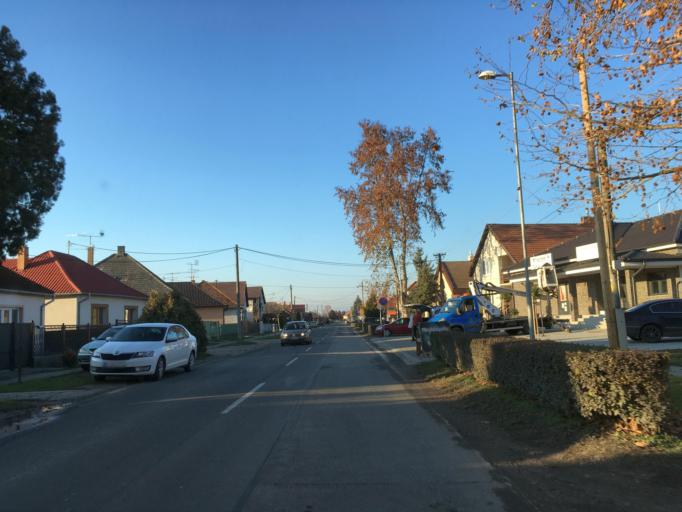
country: SK
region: Trnavsky
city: Gabcikovo
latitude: 47.8952
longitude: 17.5750
